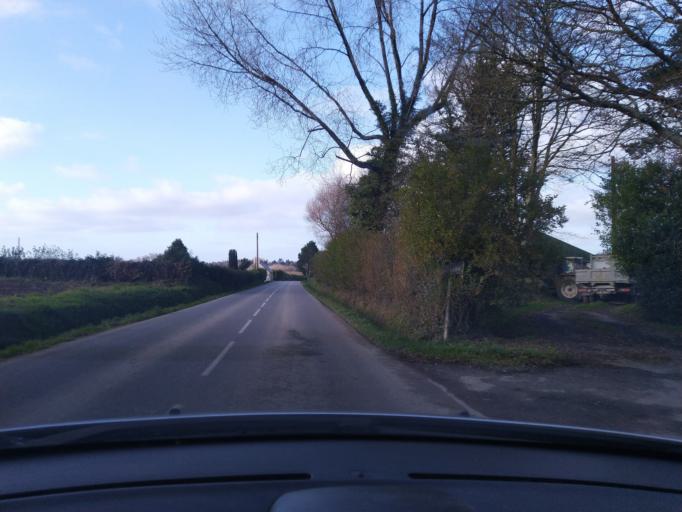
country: FR
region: Brittany
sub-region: Departement du Finistere
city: Plouigneau
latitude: 48.5563
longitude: -3.6908
